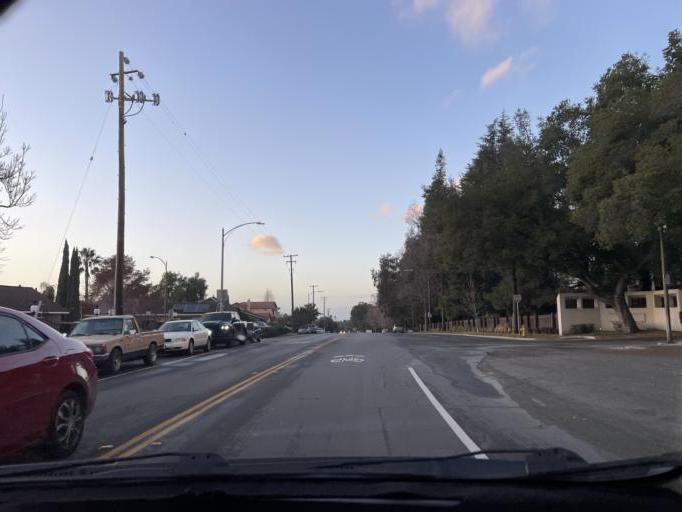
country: US
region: California
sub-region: Santa Clara County
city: Alum Rock
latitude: 37.3489
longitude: -121.7945
